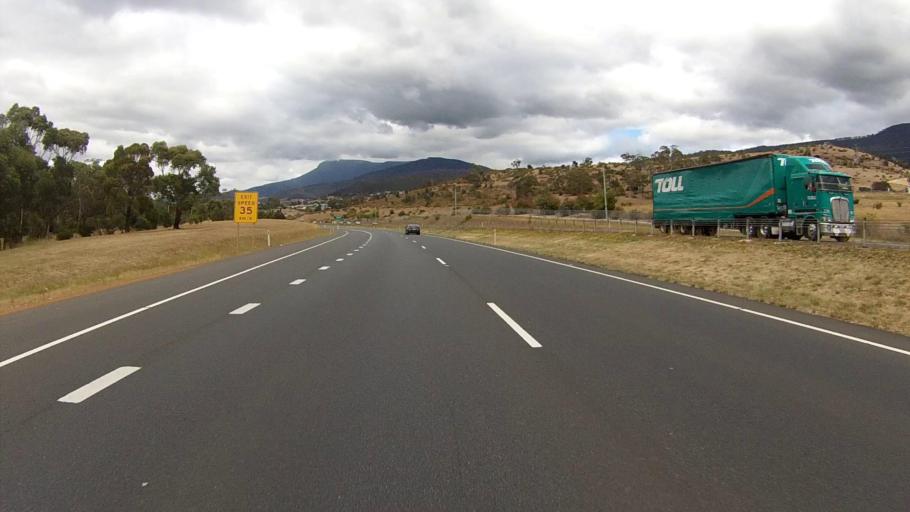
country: AU
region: Tasmania
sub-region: Glenorchy
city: Claremont
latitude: -42.7774
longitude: 147.2385
